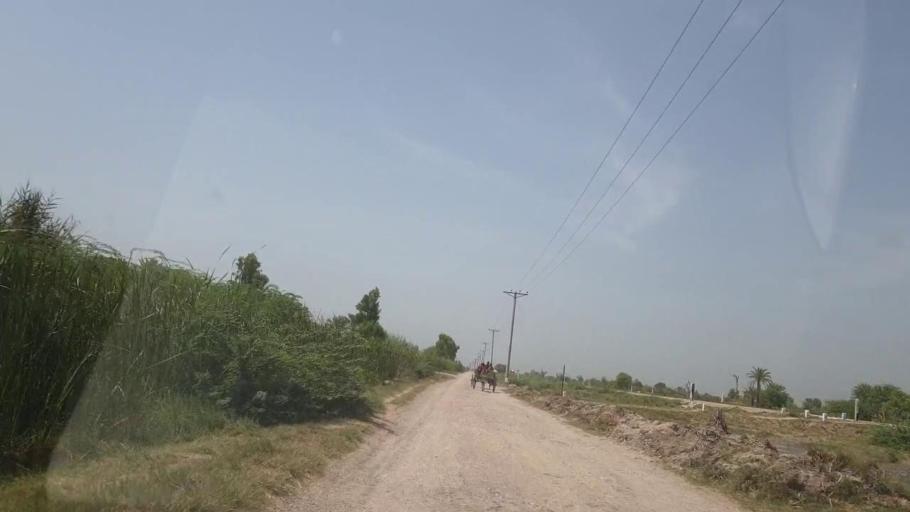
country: PK
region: Sindh
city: Gambat
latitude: 27.3295
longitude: 68.5406
